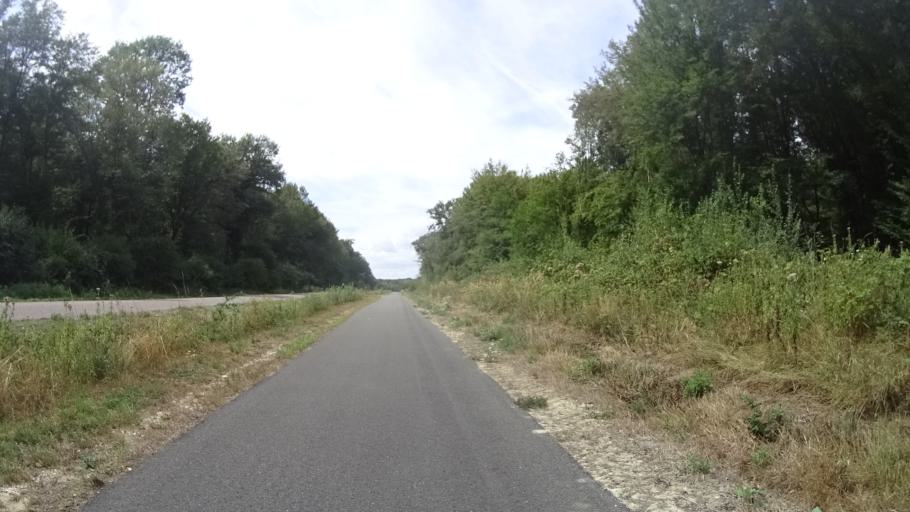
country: FR
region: Franche-Comte
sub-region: Departement du Jura
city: Damparis
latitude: 47.0762
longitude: 5.4024
